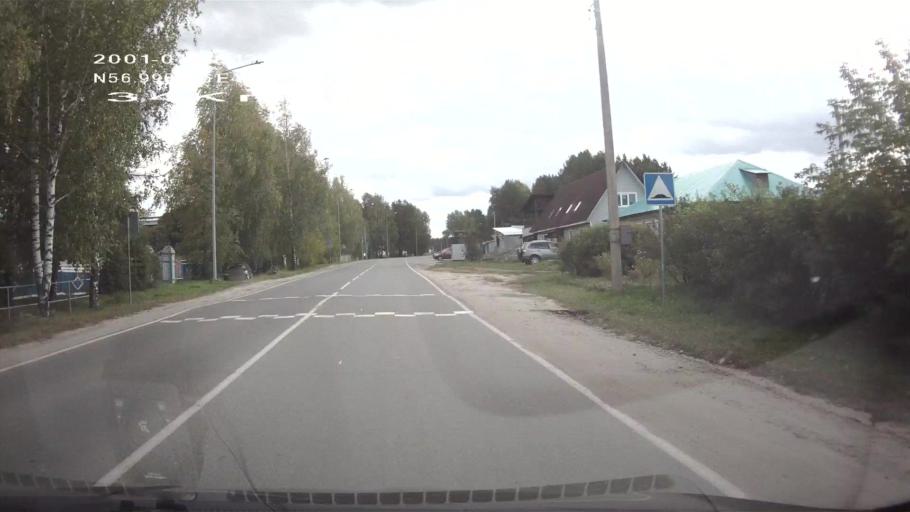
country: RU
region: Mariy-El
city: Kuzhener
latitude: 56.9984
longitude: 48.7407
